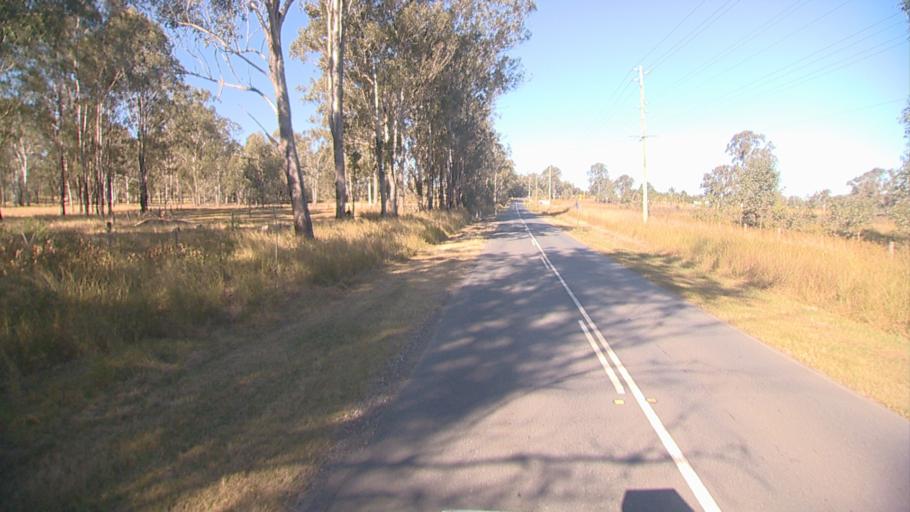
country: AU
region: Queensland
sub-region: Logan
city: North Maclean
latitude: -27.7654
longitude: 152.9984
